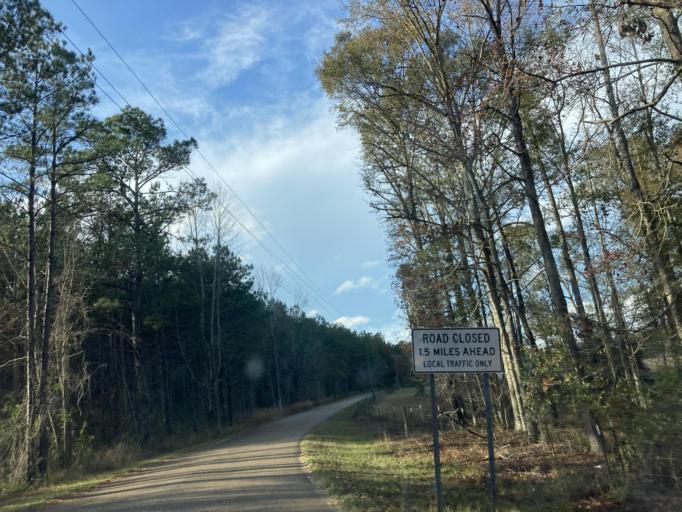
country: US
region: Mississippi
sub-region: Marion County
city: Columbia
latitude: 31.1421
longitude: -89.6410
